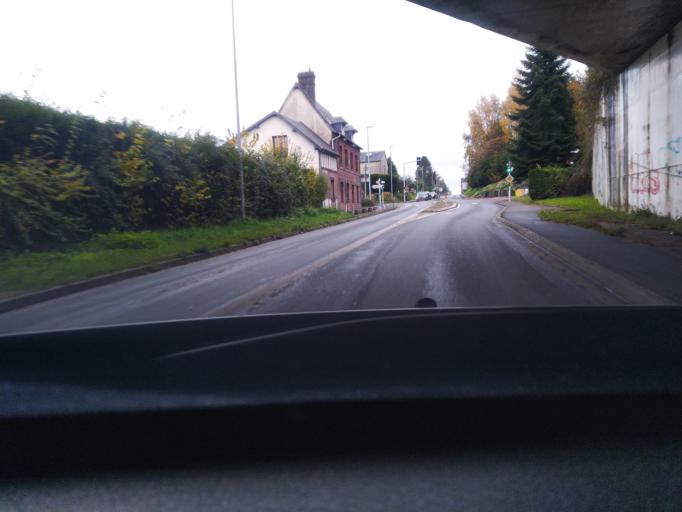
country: FR
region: Haute-Normandie
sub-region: Departement de la Seine-Maritime
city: La Vaupaliere
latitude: 49.4908
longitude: 0.9996
